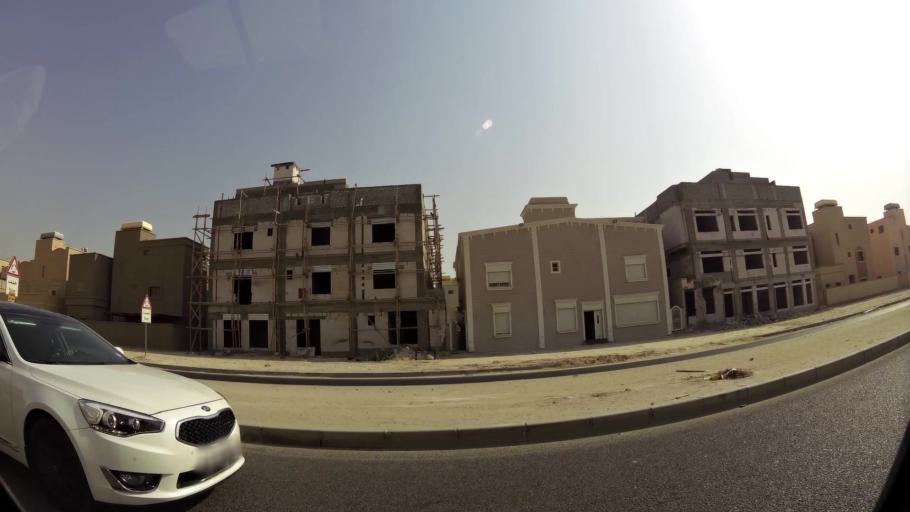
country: KW
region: Muhafazat al Jahra'
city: Al Jahra'
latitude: 29.3560
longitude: 47.7562
